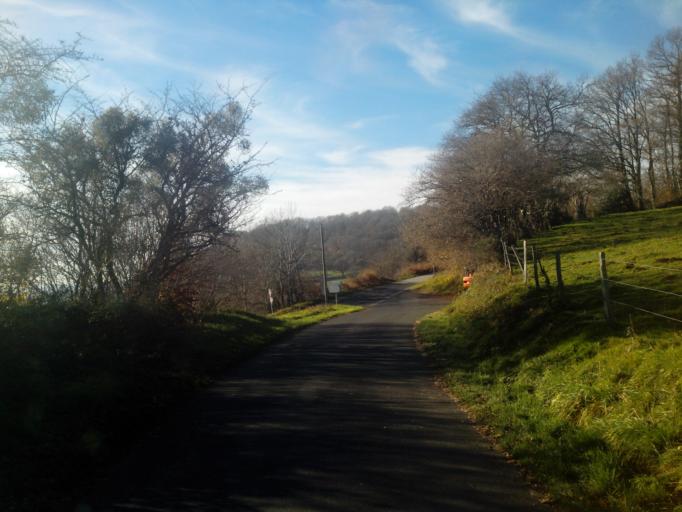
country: FR
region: Limousin
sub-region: Departement de la Correze
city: Bort-les-Orgues
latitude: 45.3977
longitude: 2.4761
